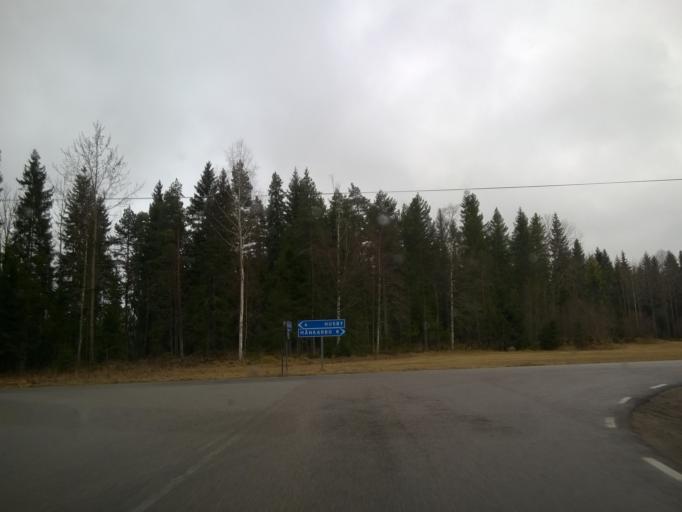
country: SE
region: Uppsala
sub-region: Osthammars Kommun
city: Bjorklinge
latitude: 60.1641
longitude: 17.5213
